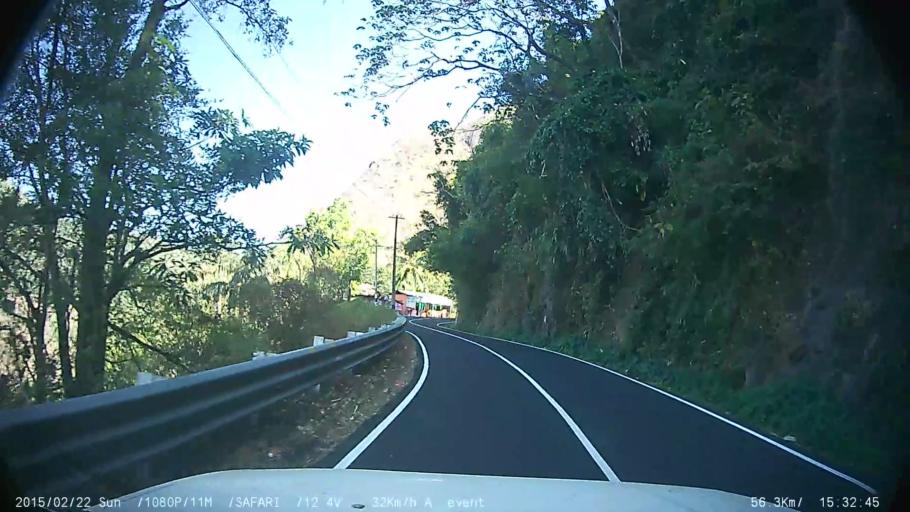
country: IN
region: Kerala
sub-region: Kottayam
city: Erattupetta
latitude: 9.5562
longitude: 76.9628
